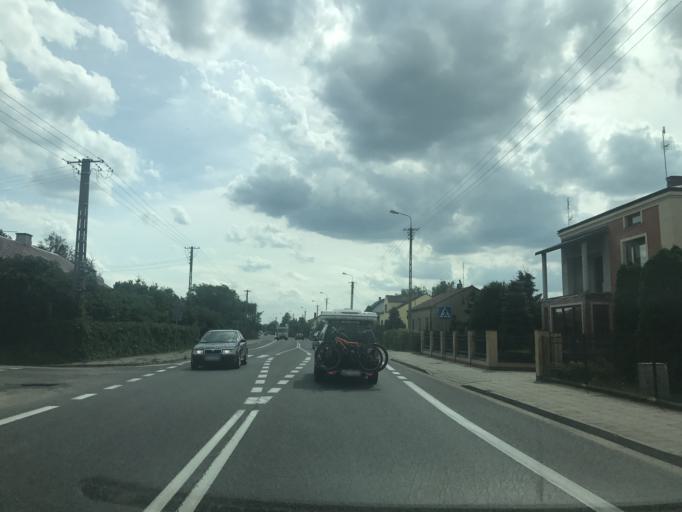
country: PL
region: Masovian Voivodeship
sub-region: Powiat mlawski
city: Wisniewo
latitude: 53.0647
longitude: 20.3481
